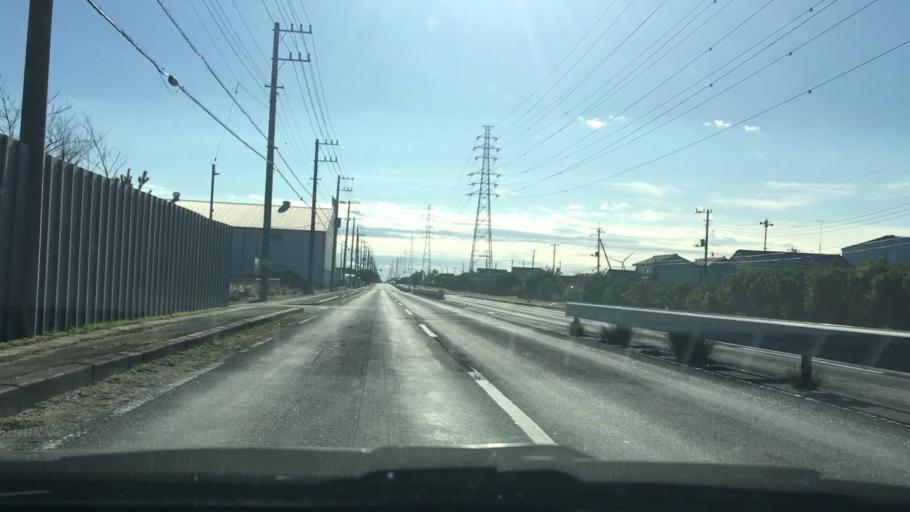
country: JP
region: Chiba
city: Omigawa
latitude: 35.8757
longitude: 140.7194
